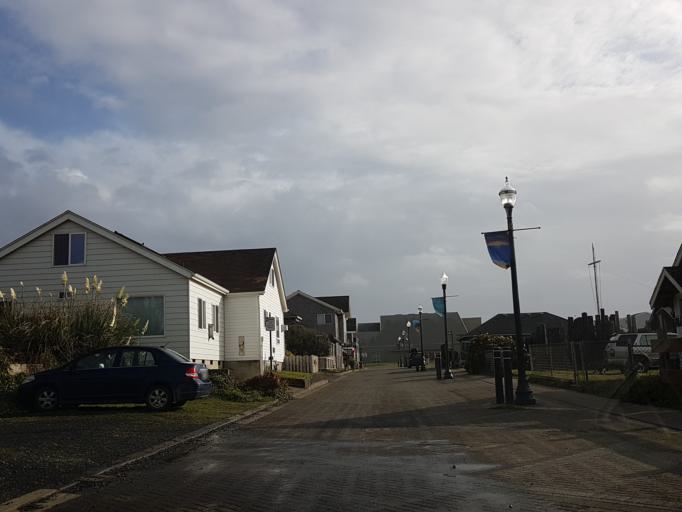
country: US
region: Oregon
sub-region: Lincoln County
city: Newport
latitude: 44.6379
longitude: -124.0619
